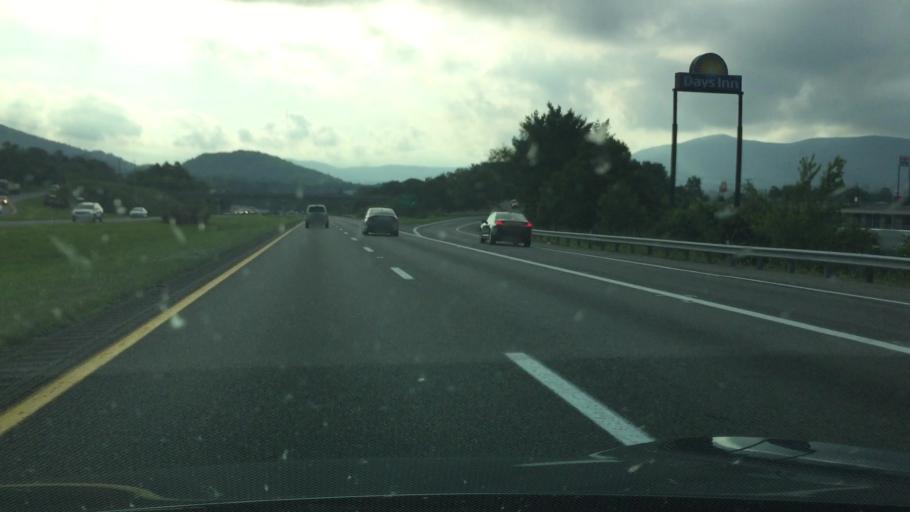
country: US
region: Virginia
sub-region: Roanoke County
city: Hollins
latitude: 37.3607
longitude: -79.9613
